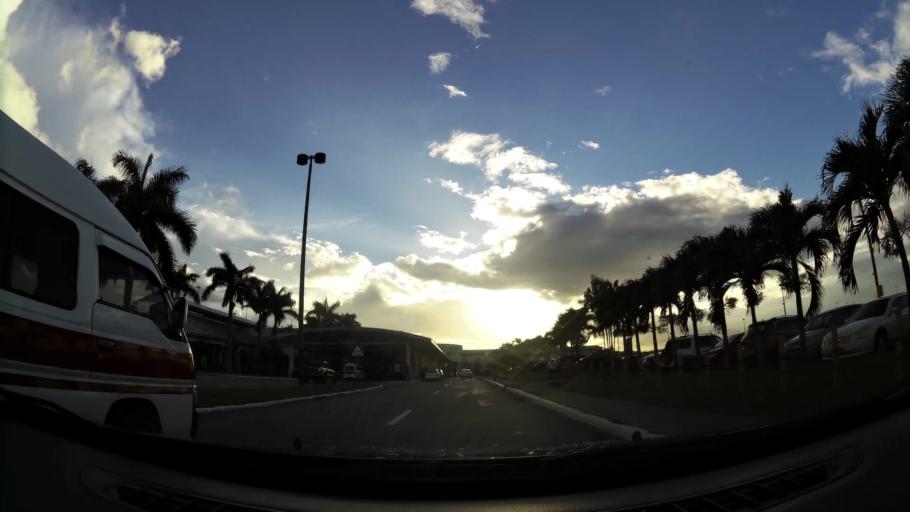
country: TT
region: Tunapuna/Piarco
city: Arouca
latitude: 10.6028
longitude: -61.3382
